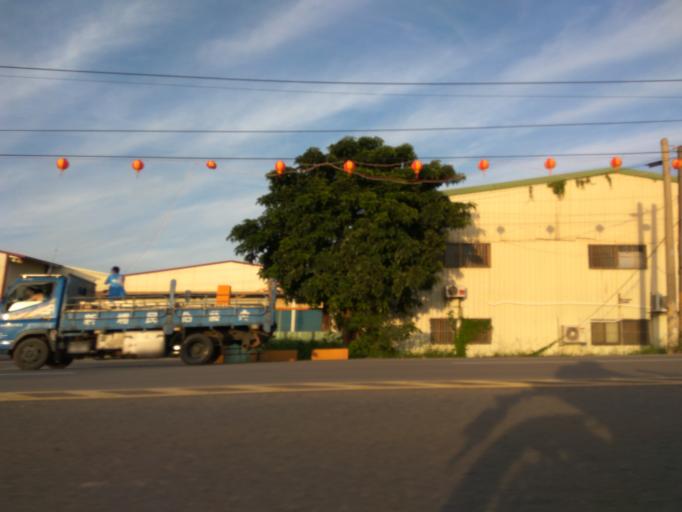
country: TW
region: Taiwan
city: Taoyuan City
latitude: 25.0083
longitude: 121.1432
